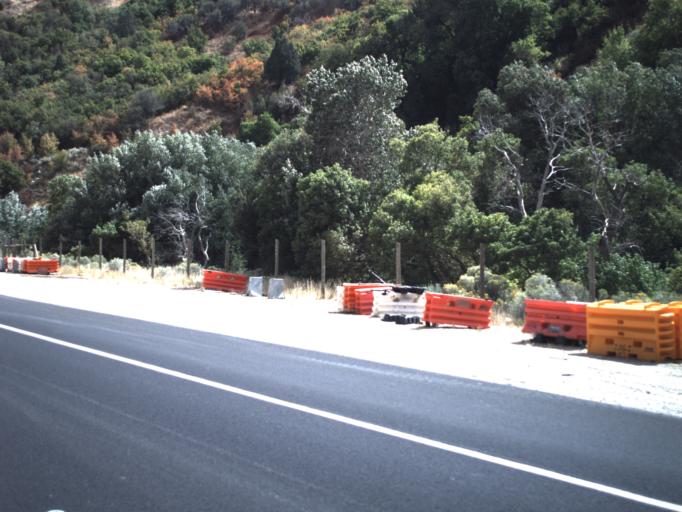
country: US
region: Utah
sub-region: Box Elder County
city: Brigham City
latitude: 41.4969
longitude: -111.9658
